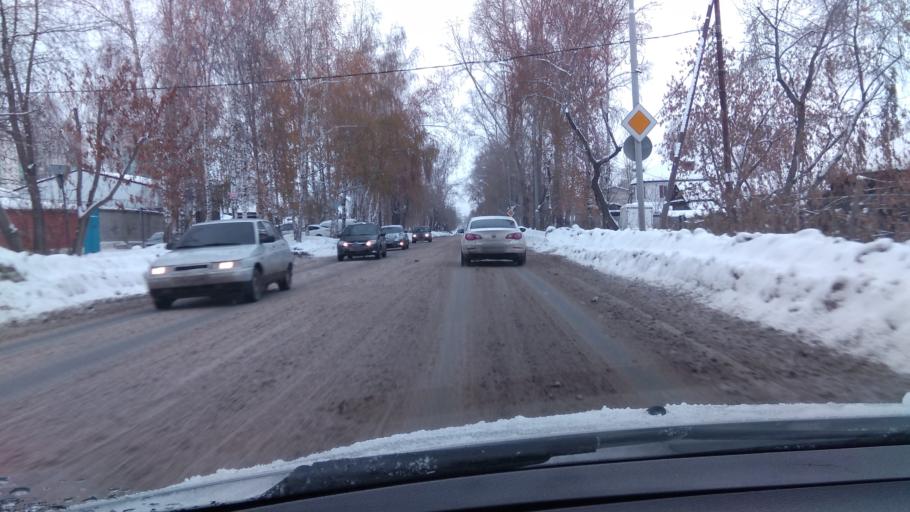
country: RU
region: Sverdlovsk
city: Yekaterinburg
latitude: 56.8095
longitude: 60.5840
